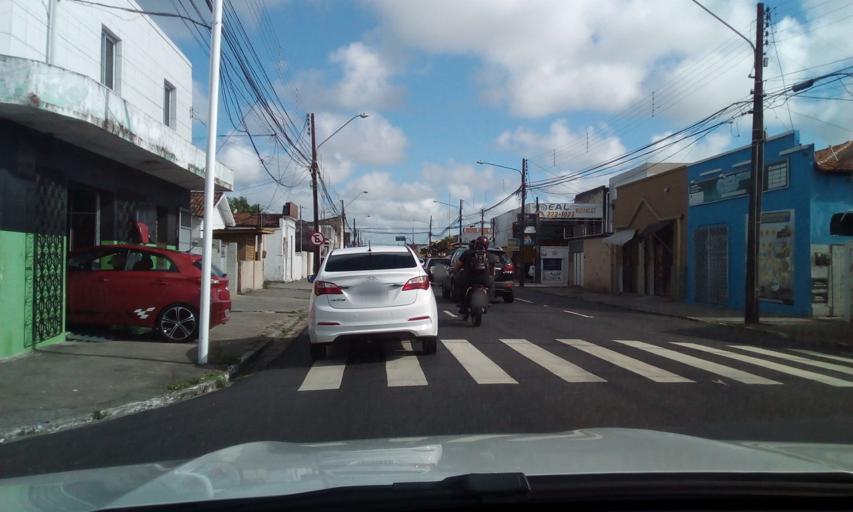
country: BR
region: Paraiba
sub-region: Joao Pessoa
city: Joao Pessoa
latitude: -7.1324
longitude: -34.8789
